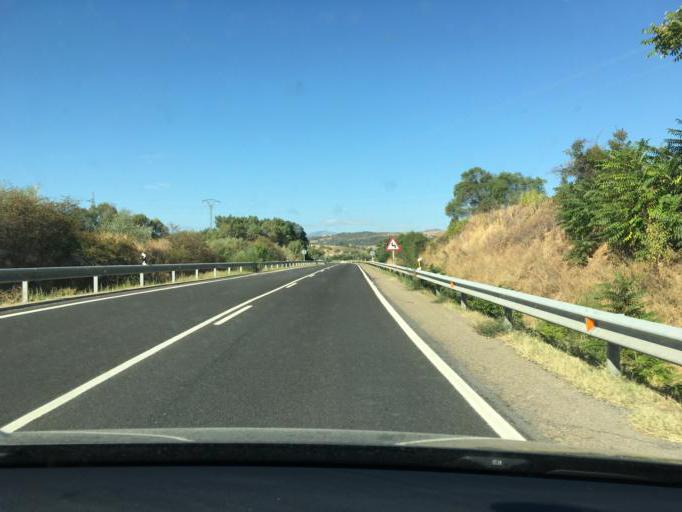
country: ES
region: Madrid
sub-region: Provincia de Madrid
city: Torrelaguna
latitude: 40.8187
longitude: -3.5644
